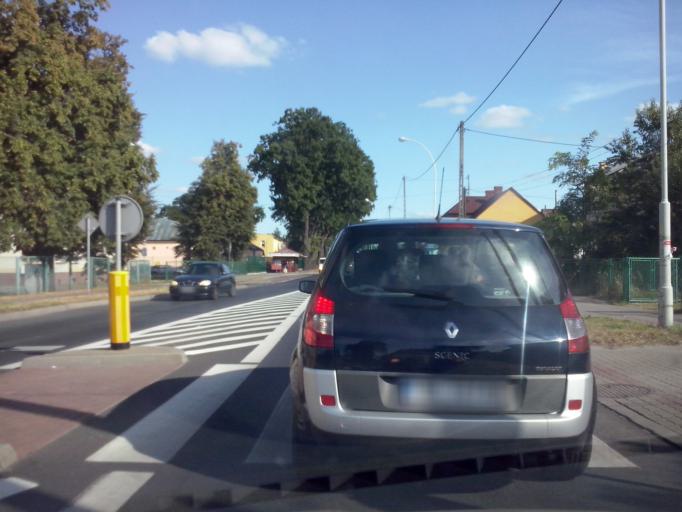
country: PL
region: Subcarpathian Voivodeship
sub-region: Powiat nizanski
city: Nisko
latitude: 50.5244
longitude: 22.1253
